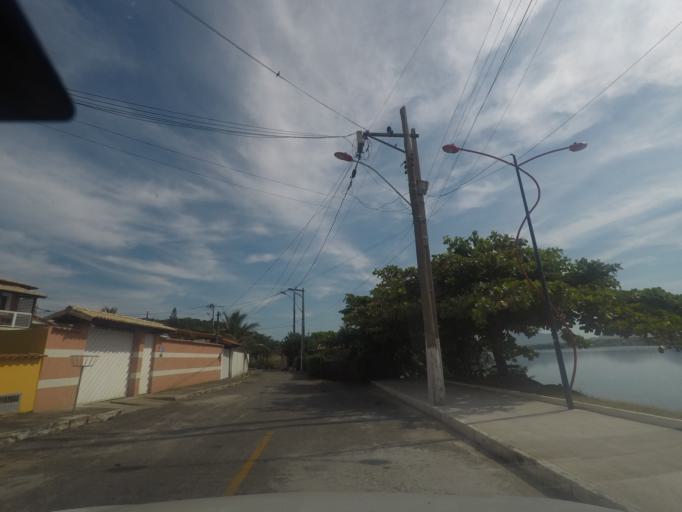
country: BR
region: Rio de Janeiro
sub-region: Marica
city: Marica
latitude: -22.9549
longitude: -42.8093
